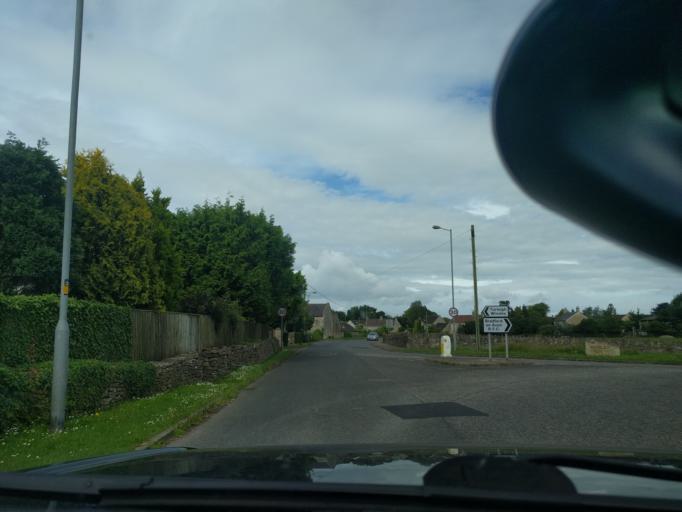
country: GB
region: England
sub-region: Wiltshire
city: Westwood
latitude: 51.3495
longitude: -2.2754
